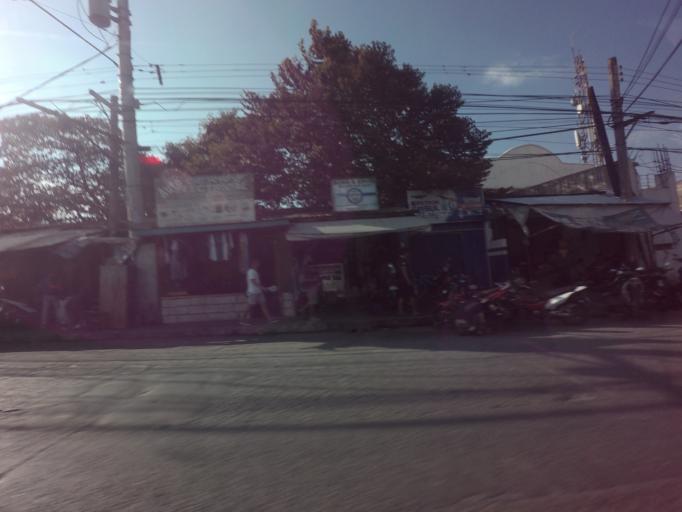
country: PH
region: Calabarzon
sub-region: Province of Rizal
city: Taguig
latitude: 14.4820
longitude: 121.0473
